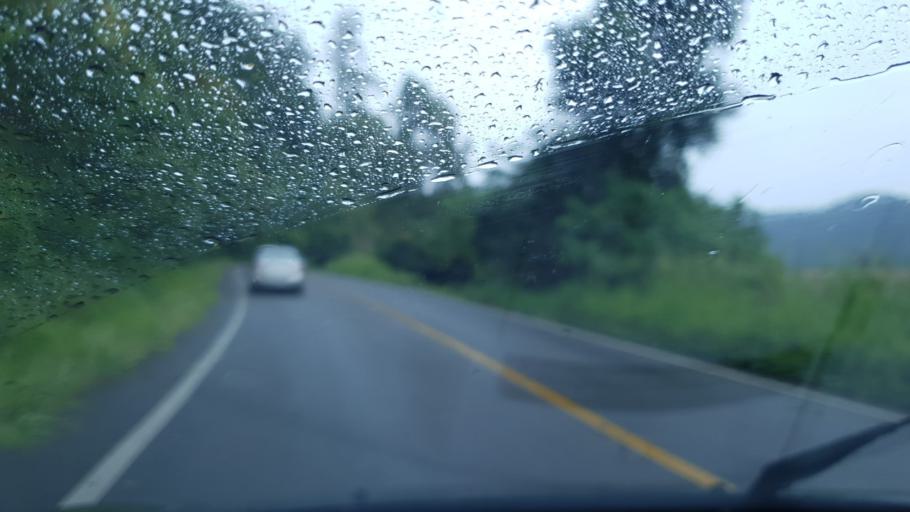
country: TH
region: Mae Hong Son
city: Khun Yuam
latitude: 18.6809
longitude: 97.9207
